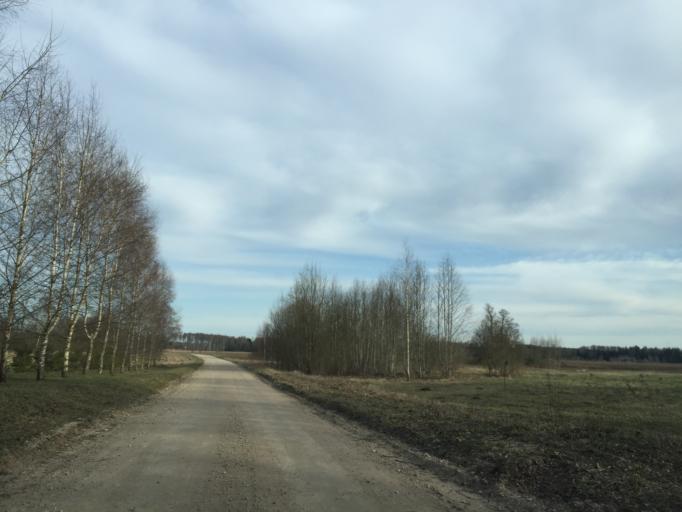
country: LV
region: Kegums
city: Kegums
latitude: 56.7984
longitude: 24.7495
